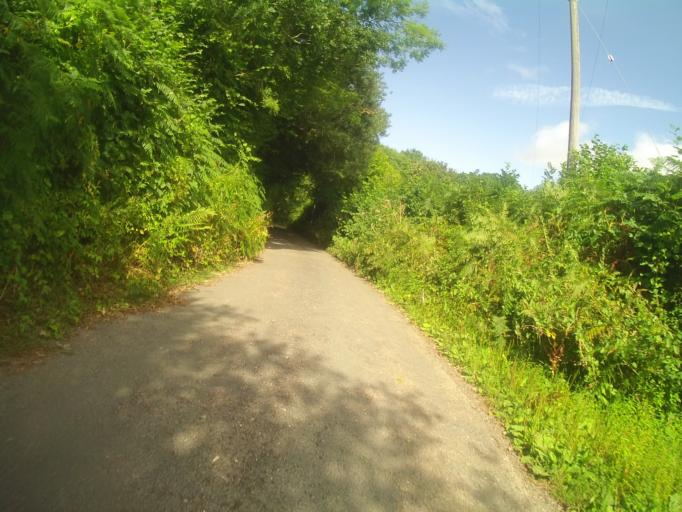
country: GB
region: England
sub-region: Devon
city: Buckfastleigh
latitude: 50.4618
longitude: -3.7590
